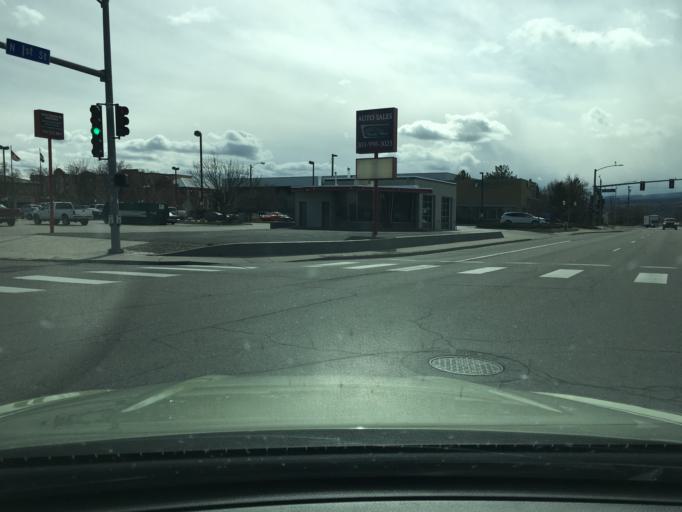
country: US
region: Colorado
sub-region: Mesa County
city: Grand Junction
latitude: 39.0684
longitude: -108.5709
